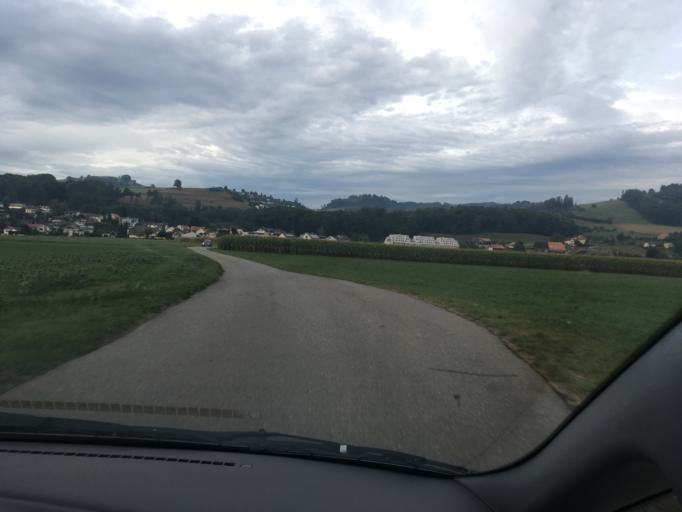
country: CH
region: Bern
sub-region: Bern-Mittelland District
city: Vechigen
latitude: 46.9476
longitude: 7.5460
